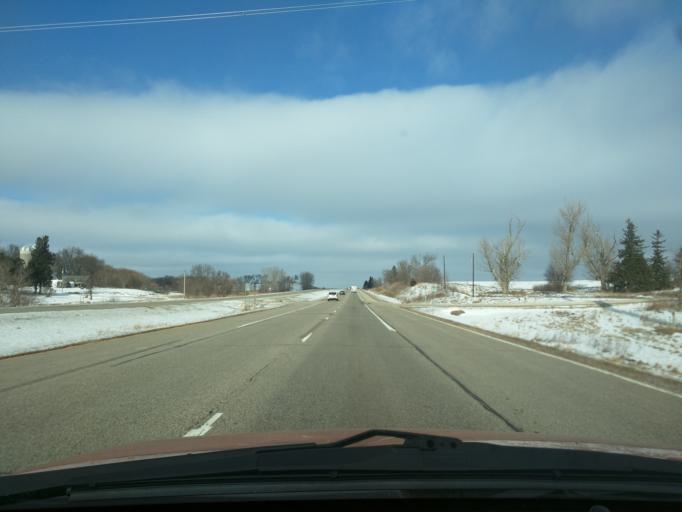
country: US
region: Minnesota
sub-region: Goodhue County
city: Pine Island
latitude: 44.2234
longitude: -92.6505
